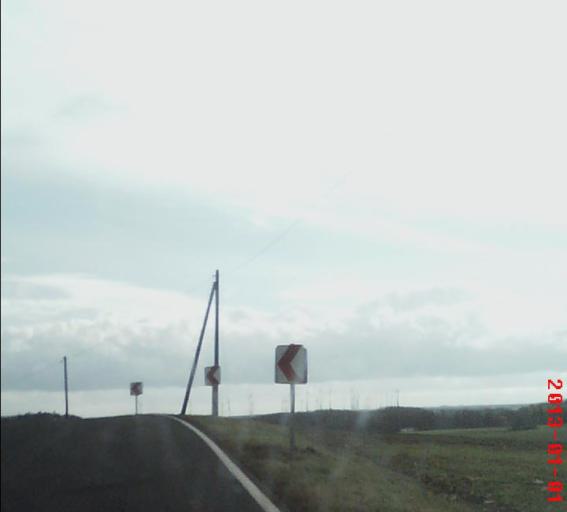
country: DE
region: Thuringia
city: Wachstedt
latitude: 51.2995
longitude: 10.2335
